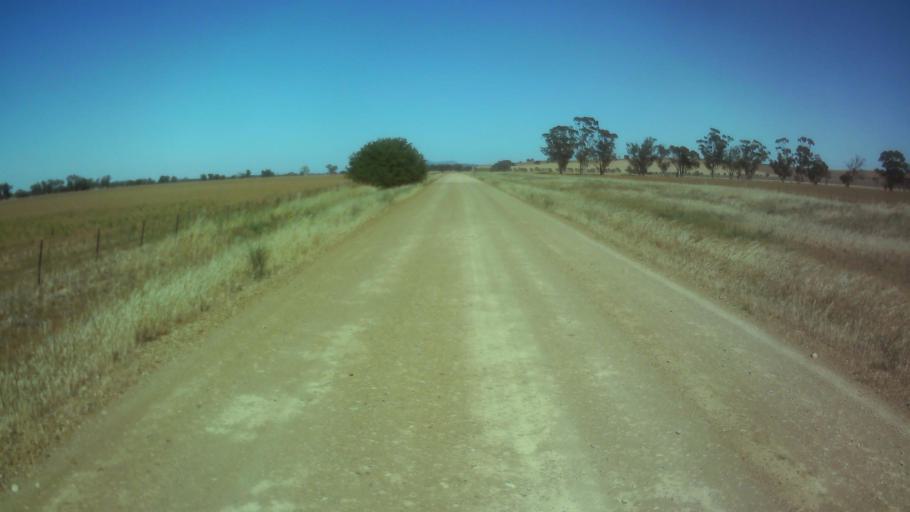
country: AU
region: New South Wales
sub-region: Weddin
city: Grenfell
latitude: -33.9960
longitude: 148.3753
